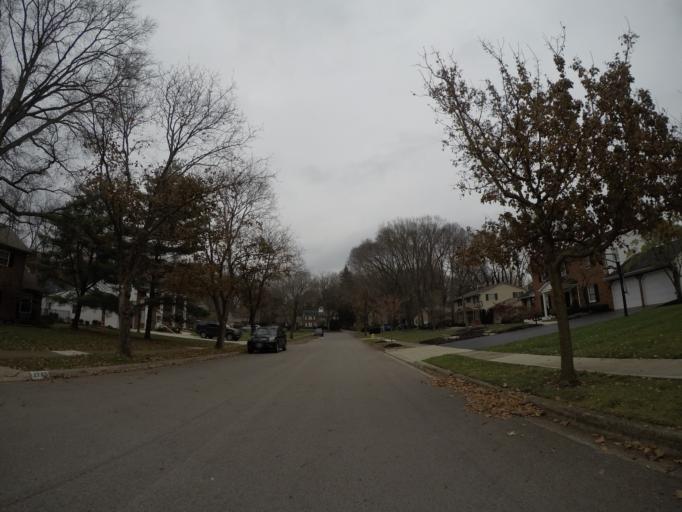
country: US
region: Ohio
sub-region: Franklin County
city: Dublin
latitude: 40.0455
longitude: -83.0919
